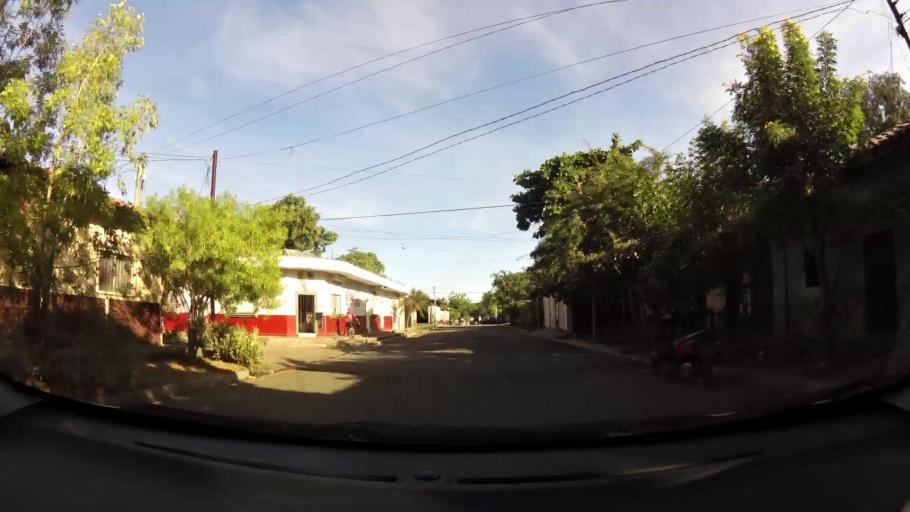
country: SV
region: San Miguel
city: San Miguel
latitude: 13.4631
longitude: -88.1757
